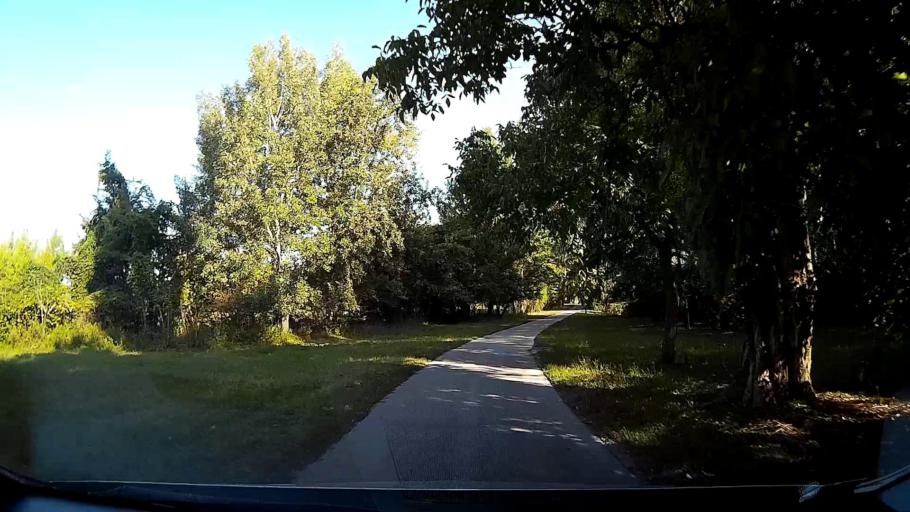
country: HU
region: Pest
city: Nagymaros
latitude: 47.7601
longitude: 18.9387
